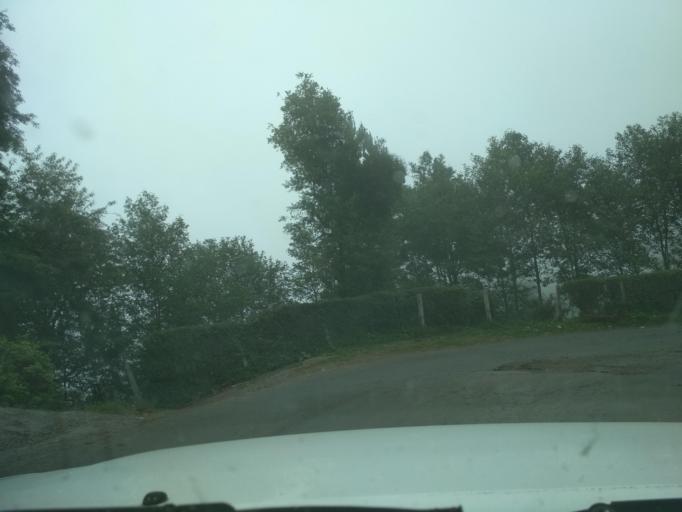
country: MX
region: Veracruz
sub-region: La Perla
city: Chilapa
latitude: 18.9746
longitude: -97.1724
